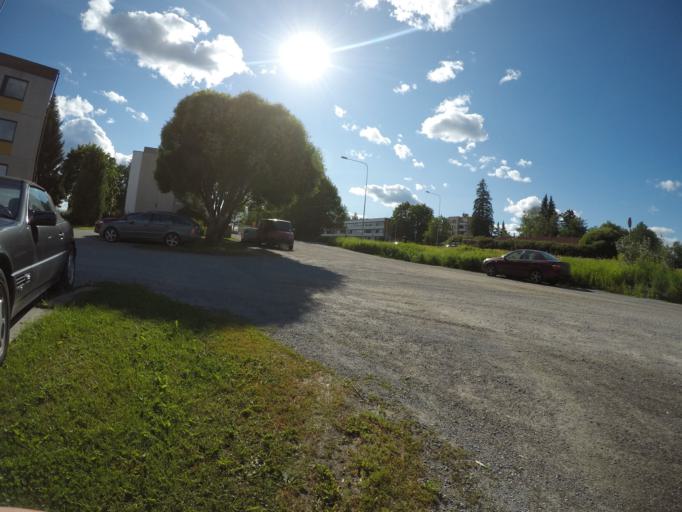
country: FI
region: Haeme
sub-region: Haemeenlinna
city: Haemeenlinna
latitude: 61.0043
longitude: 24.5011
